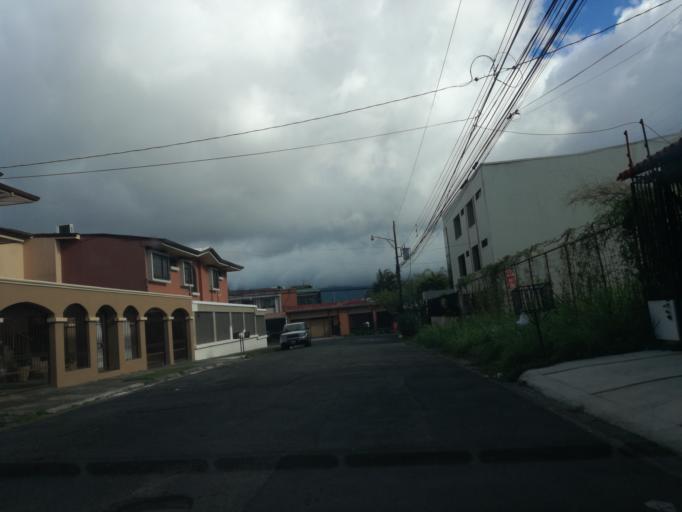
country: CR
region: San Jose
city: San Pedro
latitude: 9.9250
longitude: -84.0434
